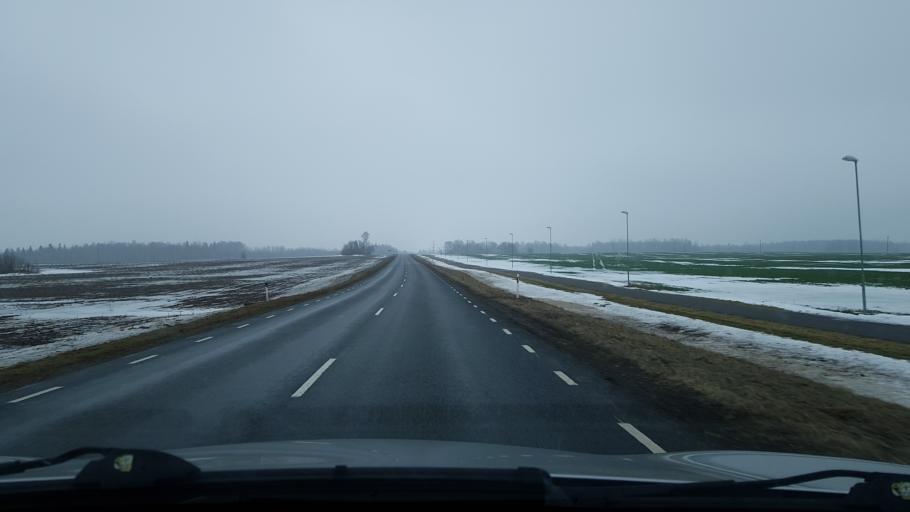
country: EE
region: Valgamaa
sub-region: Torva linn
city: Torva
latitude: 58.2178
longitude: 25.9067
